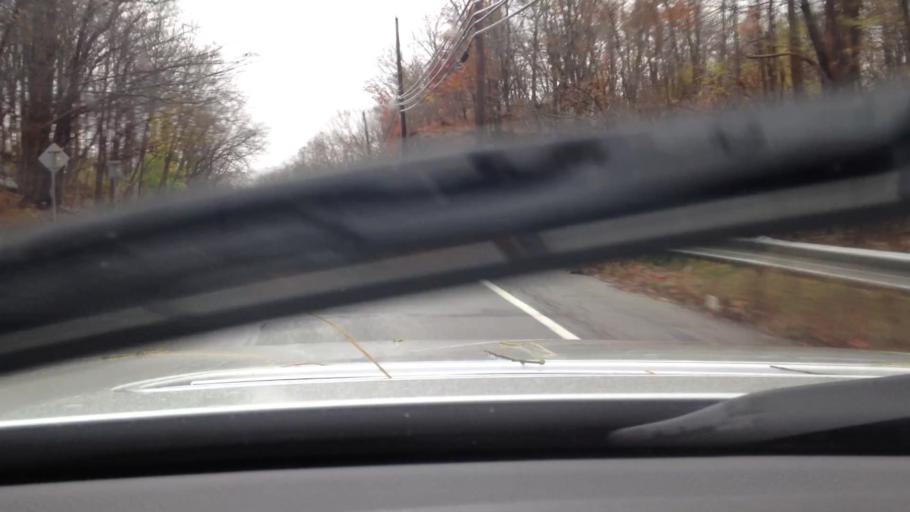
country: US
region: New York
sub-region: Westchester County
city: Peekskill
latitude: 41.3179
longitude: -73.9305
